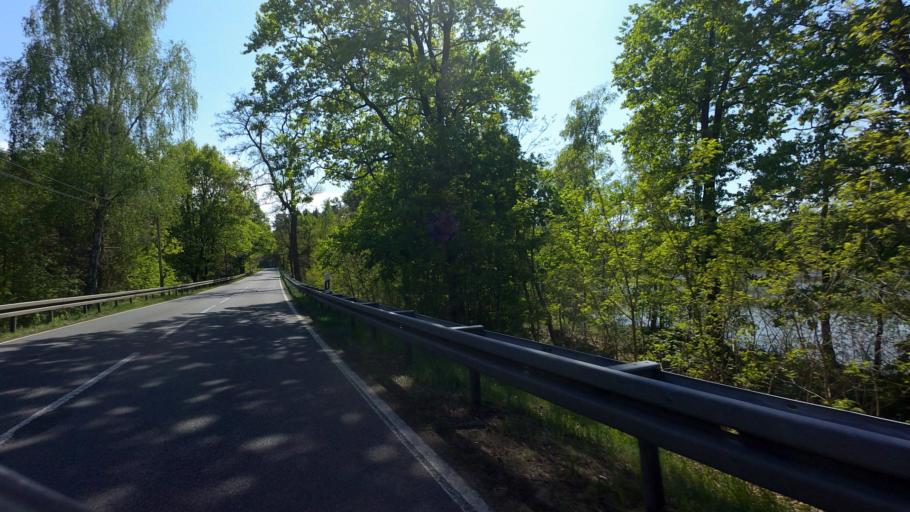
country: DE
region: Brandenburg
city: Lieberose
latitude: 51.9962
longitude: 14.2036
